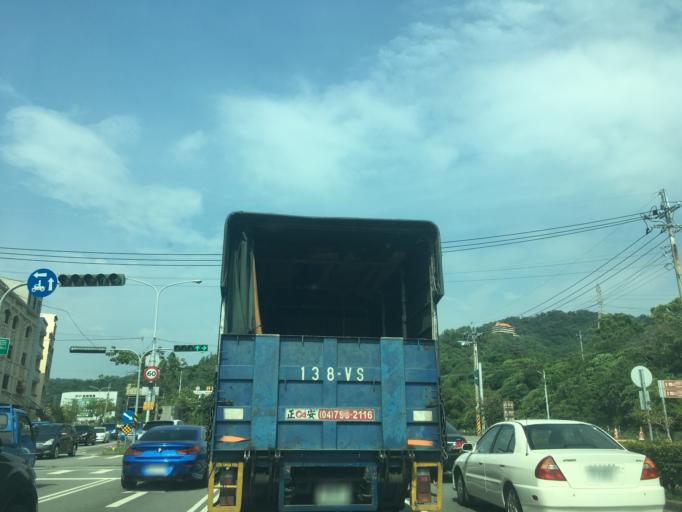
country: TW
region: Taiwan
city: Fengyuan
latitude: 24.2465
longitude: 120.7347
